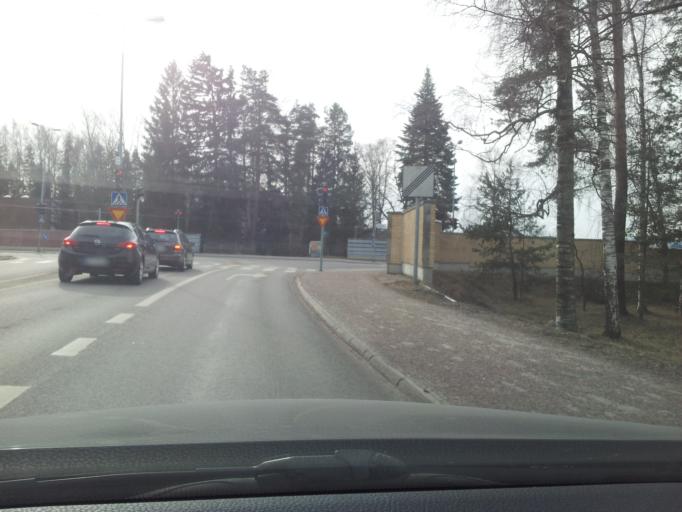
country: FI
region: Uusimaa
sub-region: Helsinki
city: Kilo
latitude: 60.1836
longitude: 24.7869
